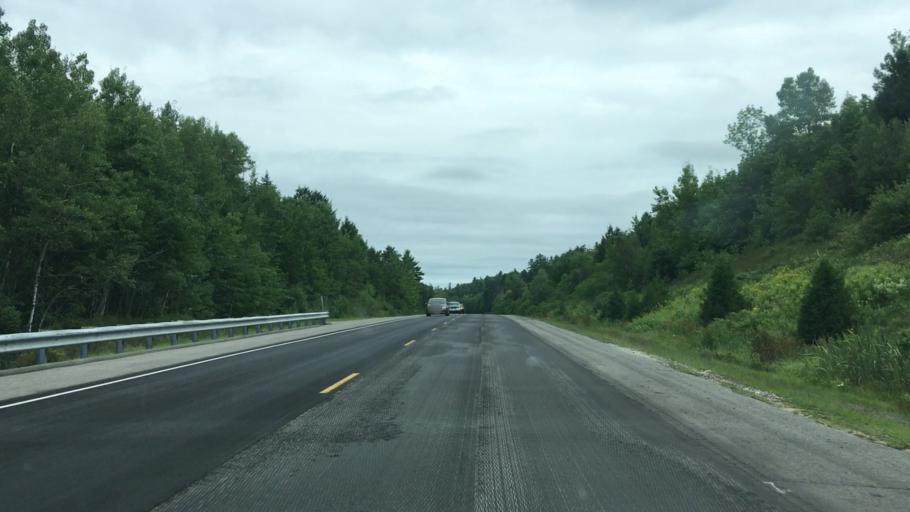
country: US
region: Maine
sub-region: Washington County
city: Cherryfield
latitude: 44.8921
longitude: -67.8562
